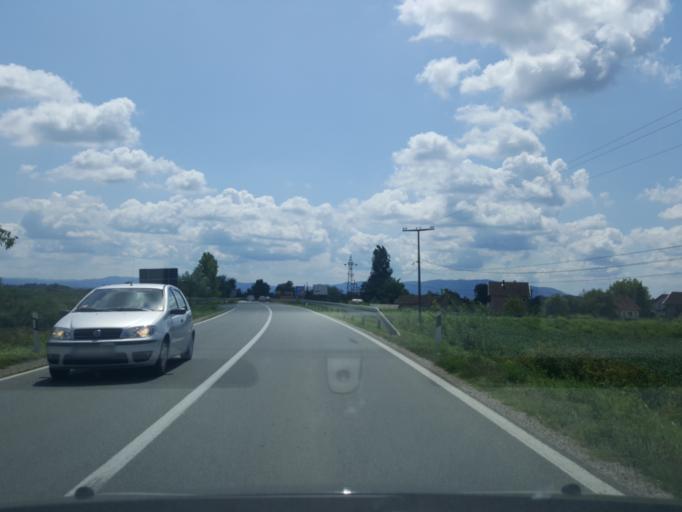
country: RS
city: Lesnica
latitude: 44.6340
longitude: 19.2741
